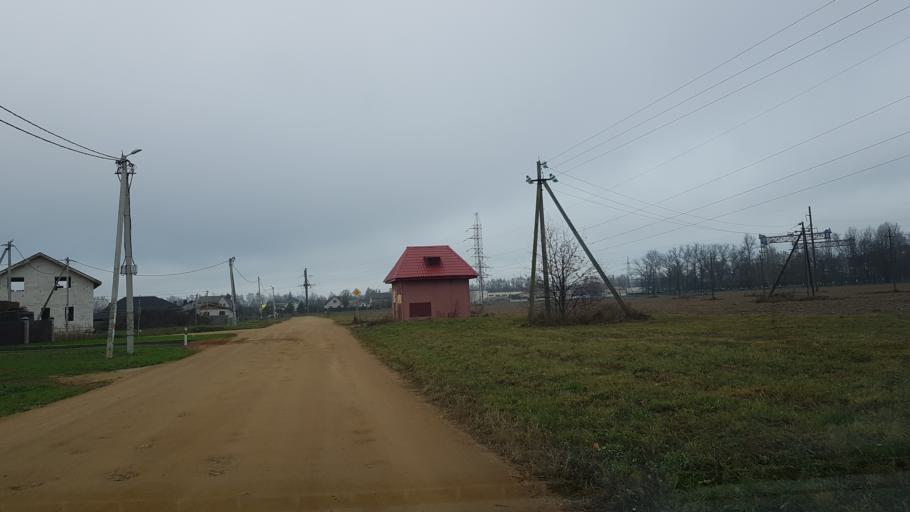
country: BY
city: Fanipol
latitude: 53.7327
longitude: 27.3270
